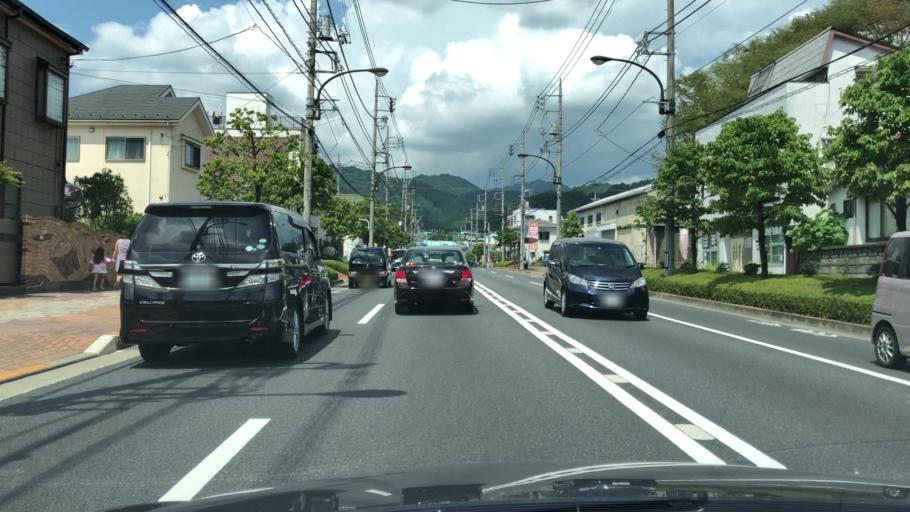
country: JP
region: Tokyo
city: Itsukaichi
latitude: 35.7303
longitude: 139.2321
